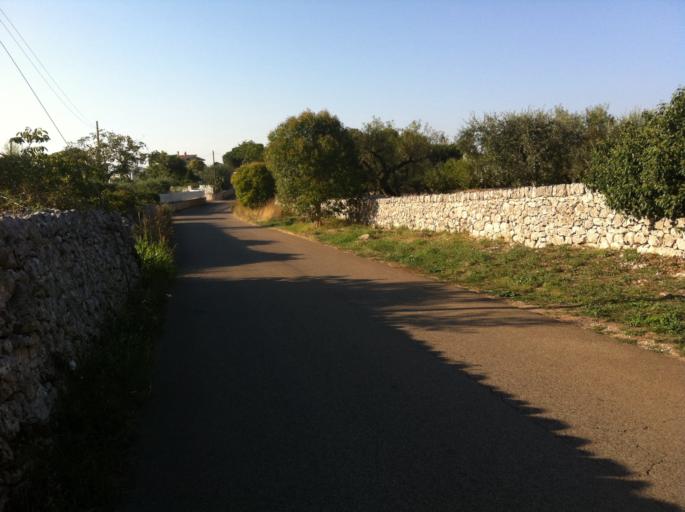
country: IT
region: Apulia
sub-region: Provincia di Bari
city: Putignano
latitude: 40.8293
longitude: 17.1340
